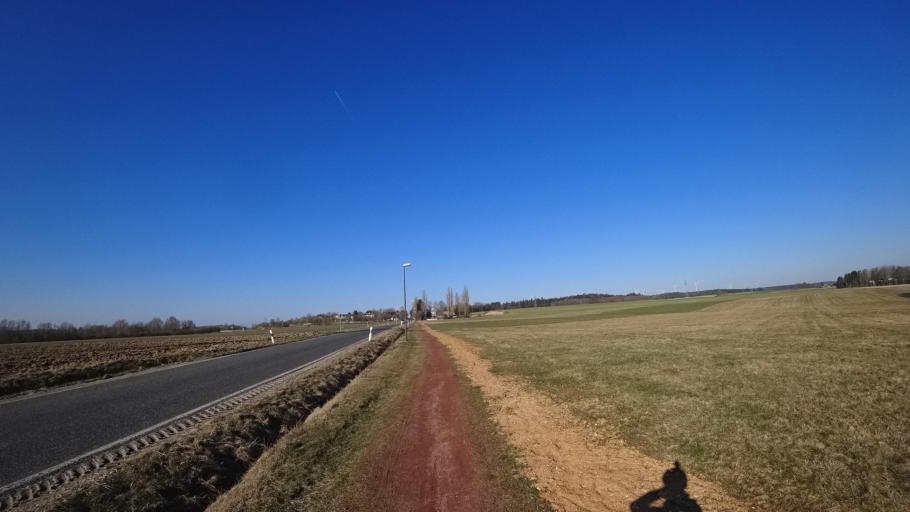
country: DE
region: Rheinland-Pfalz
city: Kumbdchen
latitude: 49.9794
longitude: 7.5084
